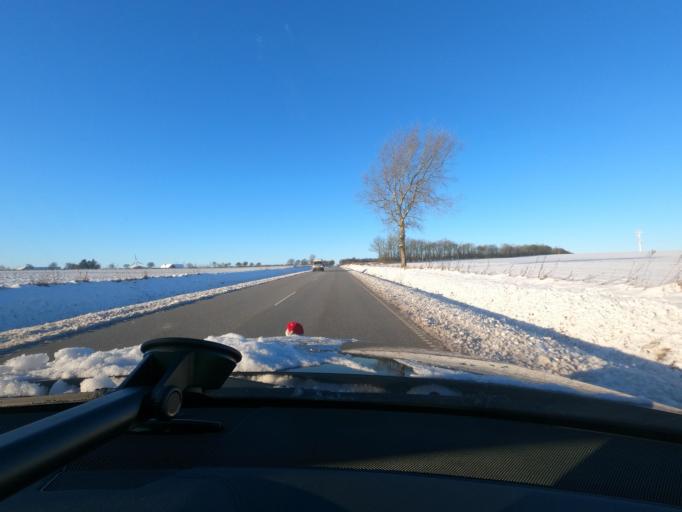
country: DK
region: South Denmark
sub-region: Aabenraa Kommune
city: Rodekro
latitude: 55.0864
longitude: 9.2122
